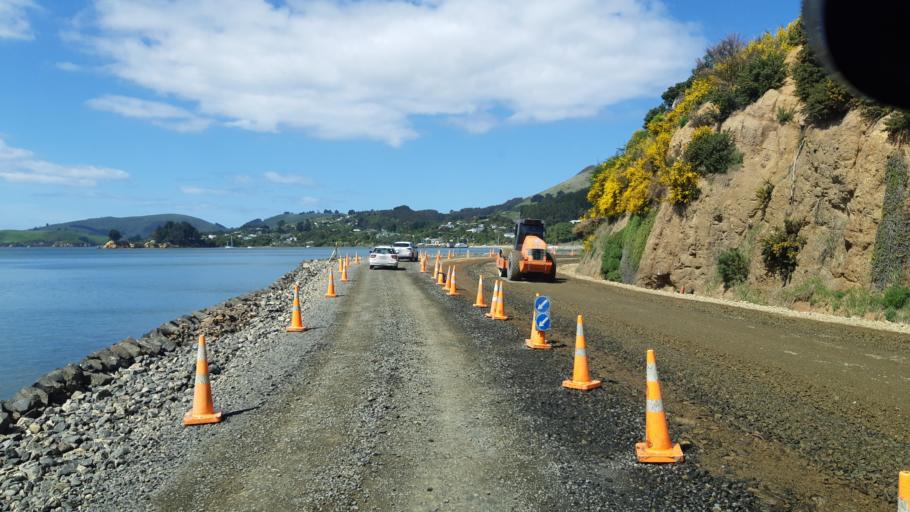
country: NZ
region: Otago
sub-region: Dunedin City
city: Portobello
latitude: -45.8477
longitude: 170.6099
